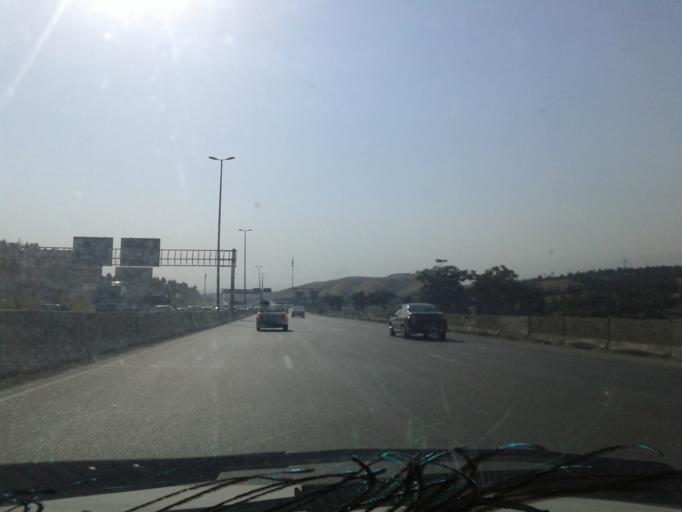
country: IR
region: Tehran
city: Tehran
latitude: 35.7313
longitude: 51.6438
